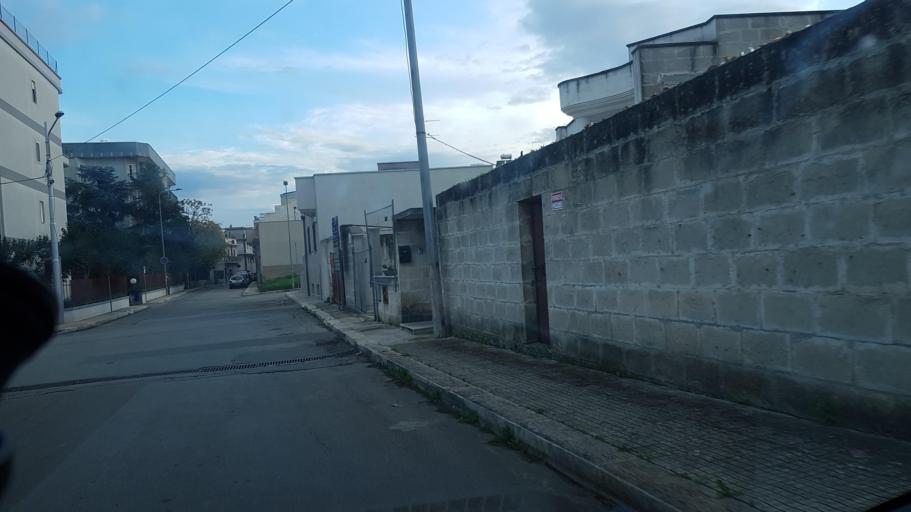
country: IT
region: Apulia
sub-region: Provincia di Brindisi
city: San Vito dei Normanni
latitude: 40.6580
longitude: 17.6974
